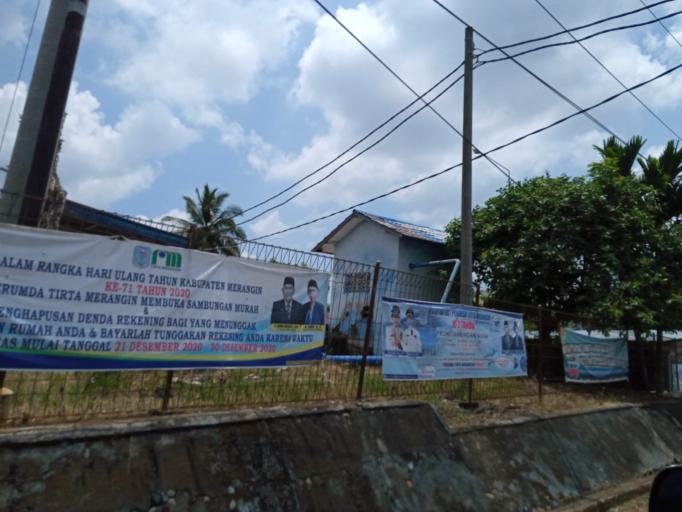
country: ID
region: Jambi
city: Bangko
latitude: -2.0861
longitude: 102.2586
